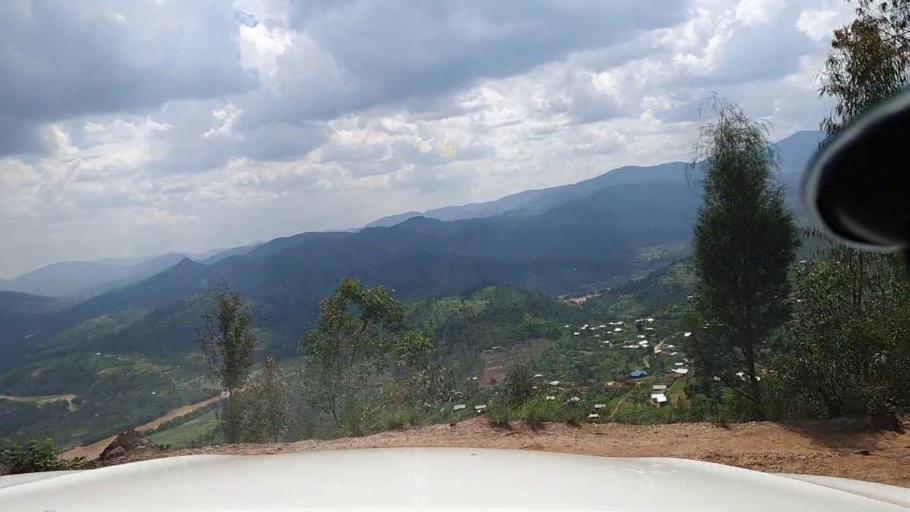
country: RW
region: Southern Province
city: Gitarama
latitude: -1.8408
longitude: 29.8195
